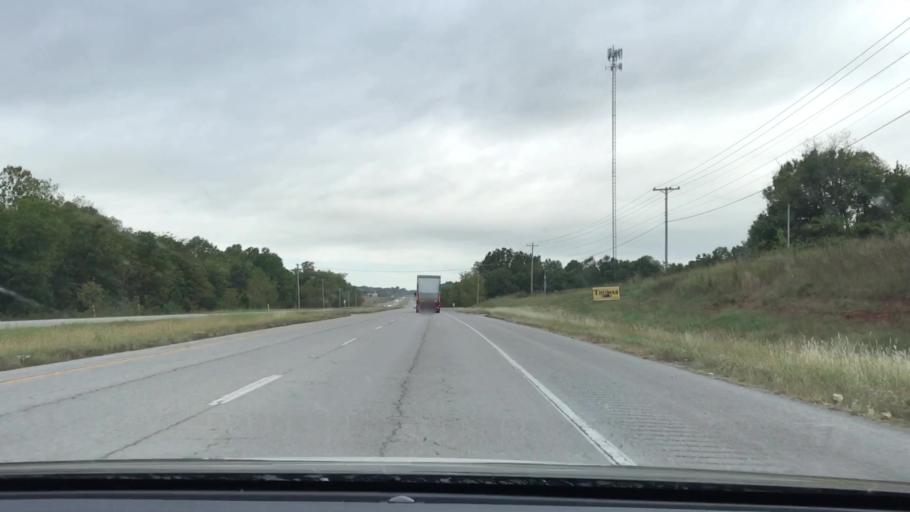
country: US
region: Kentucky
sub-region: Christian County
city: Hopkinsville
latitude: 36.8310
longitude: -87.5209
